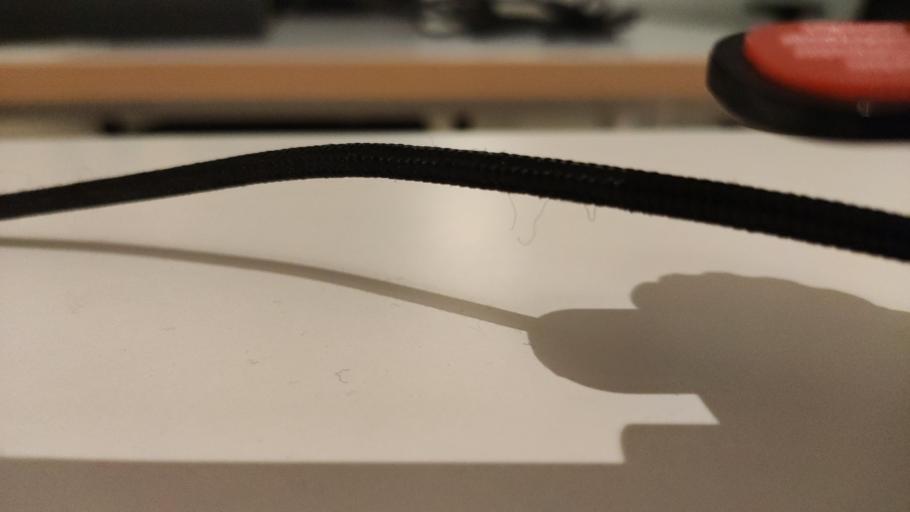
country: RU
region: Moskovskaya
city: Skoropuskovskiy
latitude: 56.3824
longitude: 38.0703
